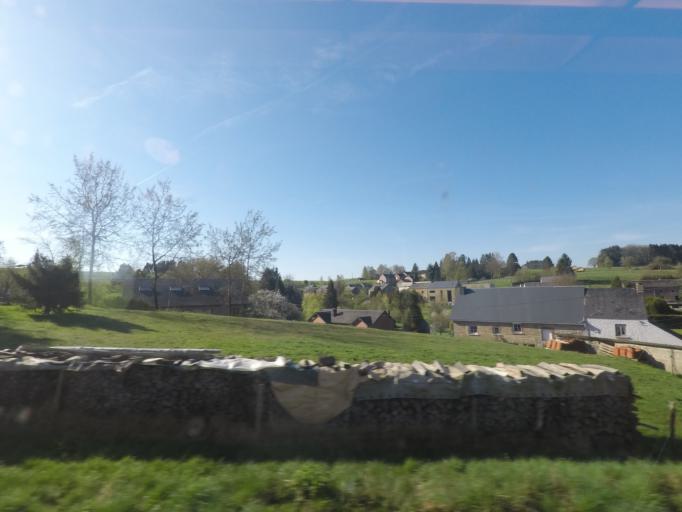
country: BE
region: Wallonia
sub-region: Province de Namur
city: Ciney
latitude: 50.2601
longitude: 5.1362
